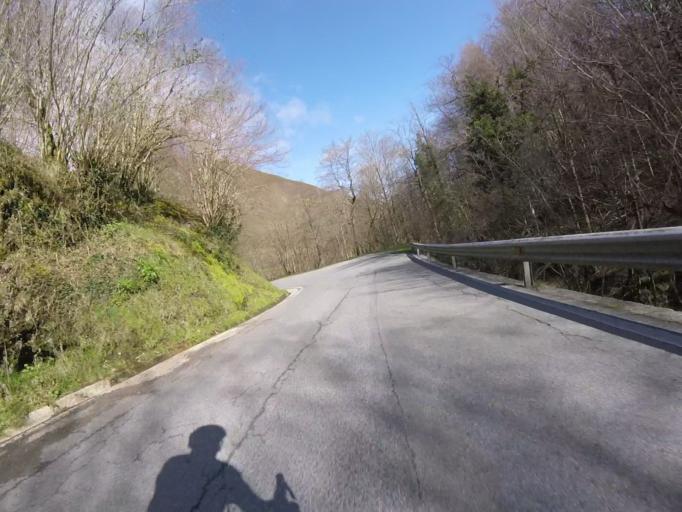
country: ES
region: Navarre
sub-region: Provincia de Navarra
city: Ezkurra
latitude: 43.0925
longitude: -1.8662
